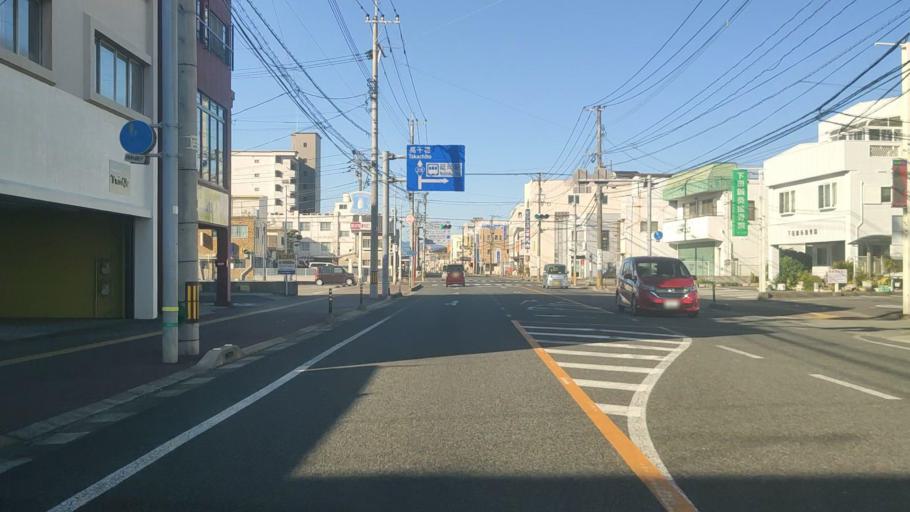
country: JP
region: Miyazaki
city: Nobeoka
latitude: 32.5853
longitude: 131.6723
